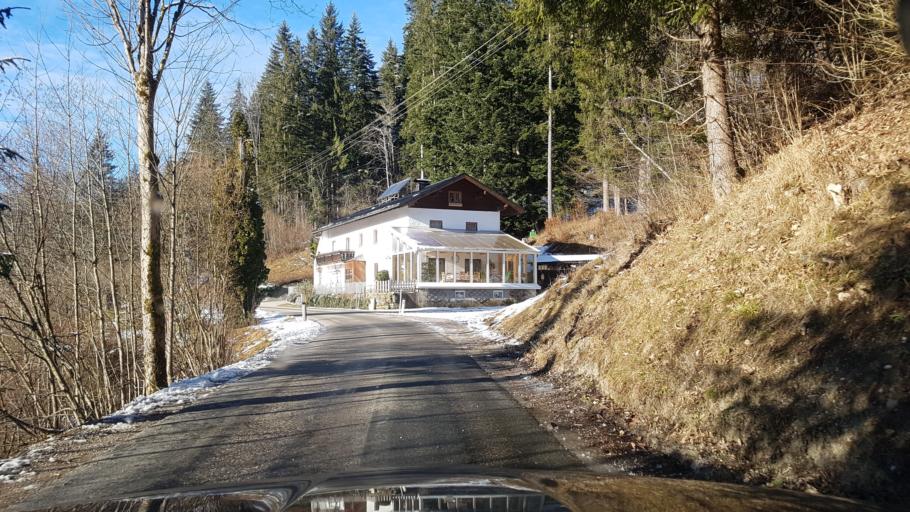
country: AT
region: Salzburg
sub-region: Politischer Bezirk Salzburg-Umgebung
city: Faistenau
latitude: 47.7757
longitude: 13.2188
